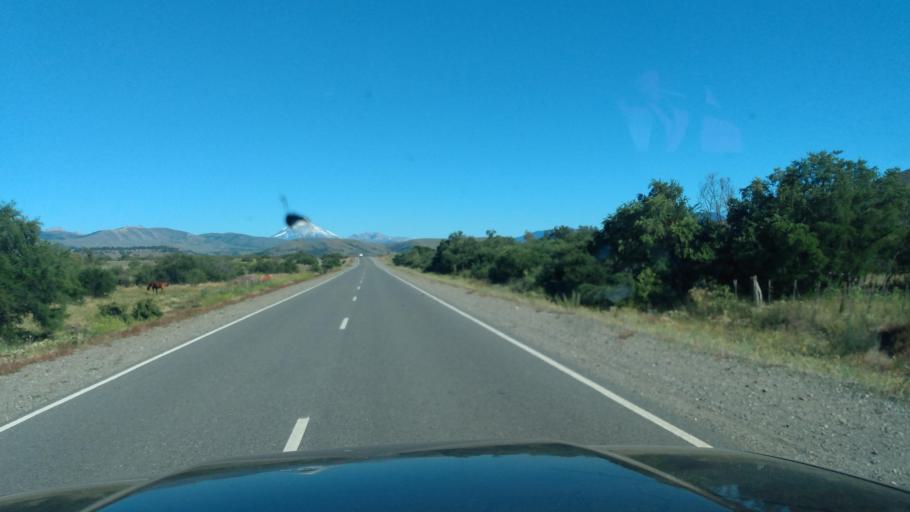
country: AR
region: Neuquen
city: Junin de los Andes
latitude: -39.8866
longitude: -71.1567
